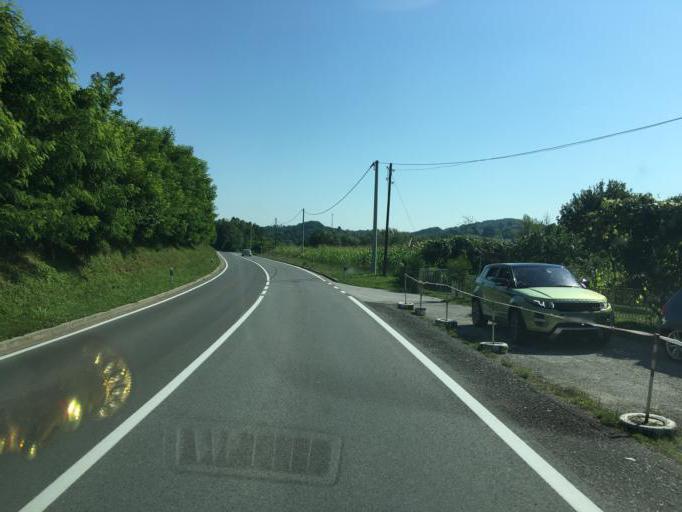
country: HR
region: Karlovacka
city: Vojnic
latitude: 45.3041
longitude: 15.6088
